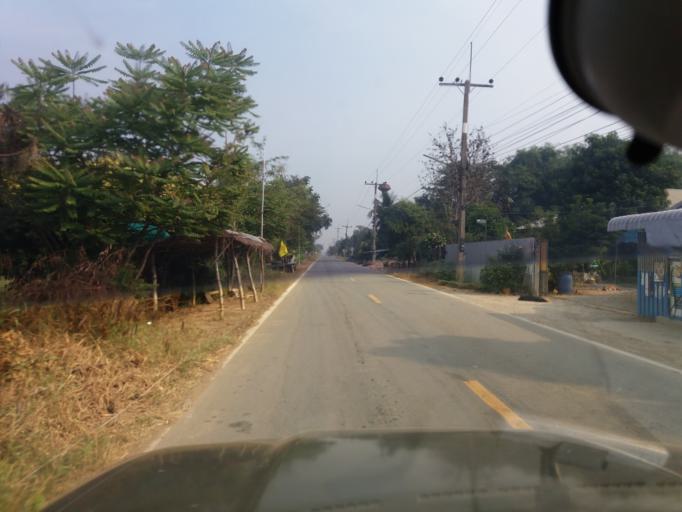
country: TH
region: Suphan Buri
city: Doem Bang Nang Buat
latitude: 14.8760
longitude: 100.1757
